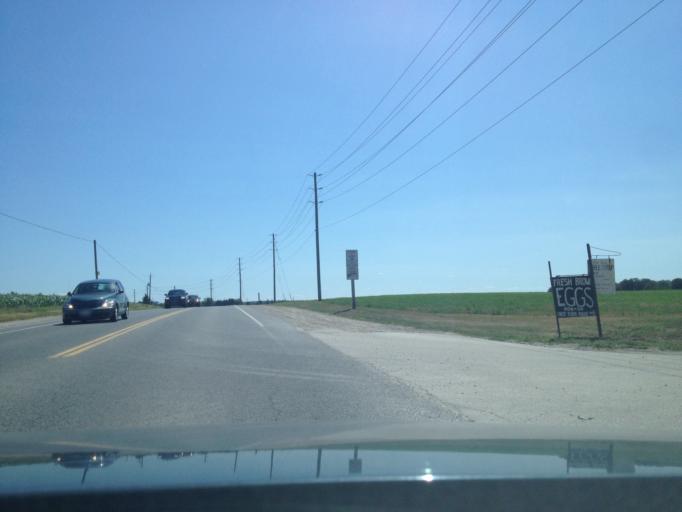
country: CA
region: Ontario
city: Waterloo
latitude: 43.5344
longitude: -80.5124
